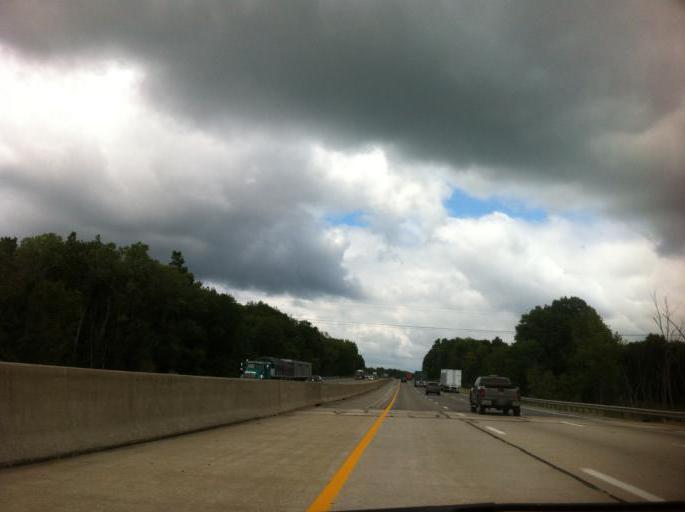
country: US
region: Ohio
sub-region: Summit County
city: Hudson
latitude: 41.2541
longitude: -81.3949
